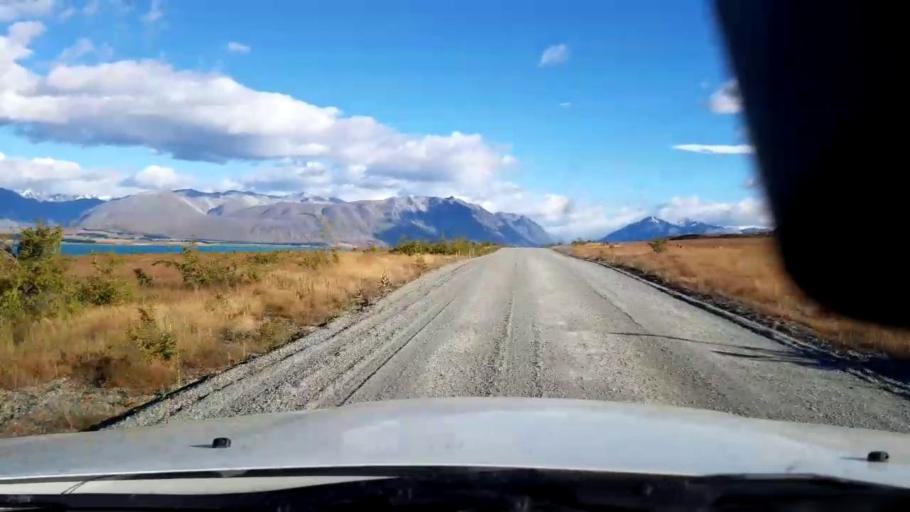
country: NZ
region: Canterbury
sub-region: Timaru District
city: Pleasant Point
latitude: -43.9169
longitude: 170.5583
